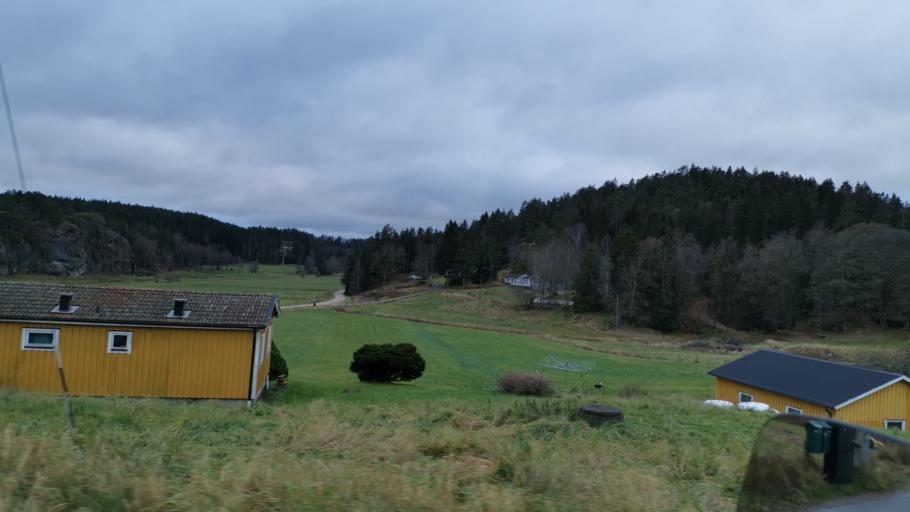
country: SE
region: Vaestra Goetaland
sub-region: Orust
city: Henan
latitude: 58.2136
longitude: 11.7256
